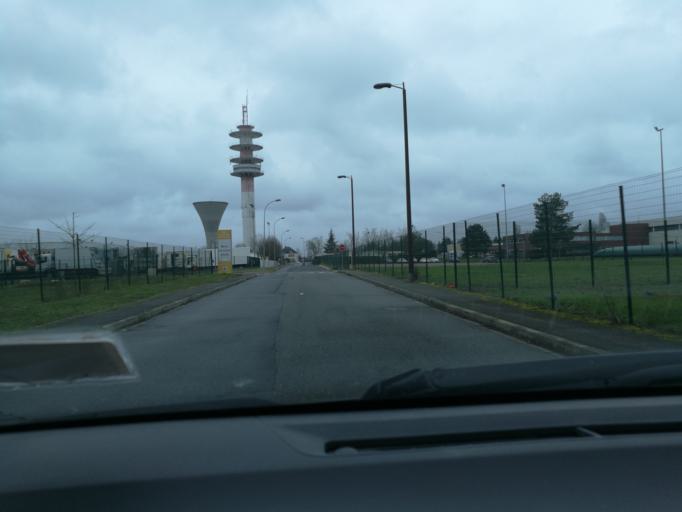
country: FR
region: Centre
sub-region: Departement du Loiret
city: Fleury-les-Aubrais
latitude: 47.9459
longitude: 1.9282
